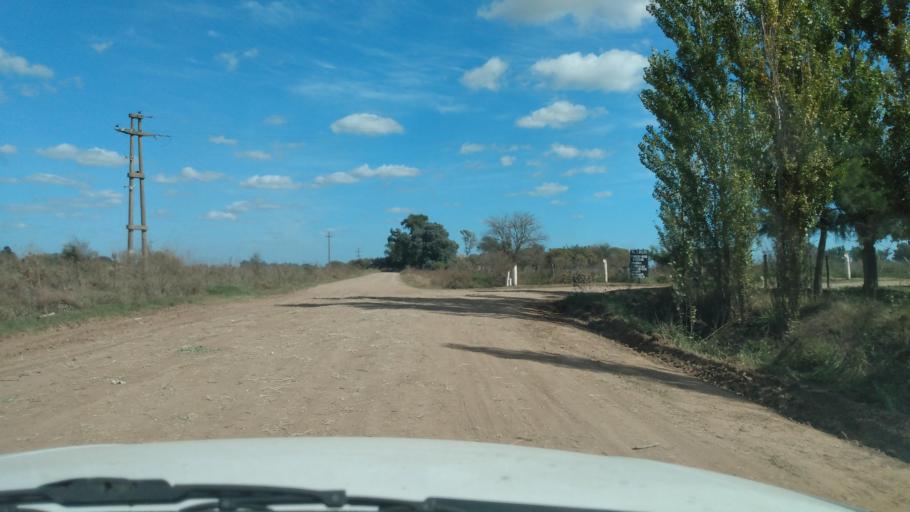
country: AR
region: Buenos Aires
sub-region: Partido de Navarro
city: Navarro
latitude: -35.0538
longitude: -59.4966
